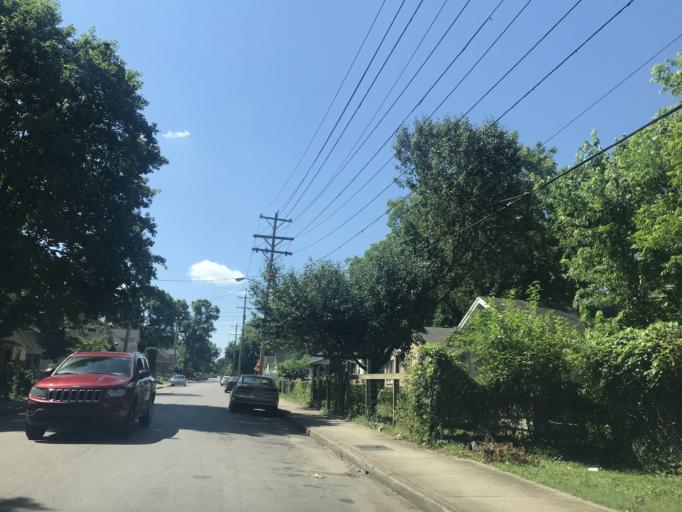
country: US
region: Tennessee
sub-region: Davidson County
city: Nashville
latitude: 36.1835
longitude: -86.8079
